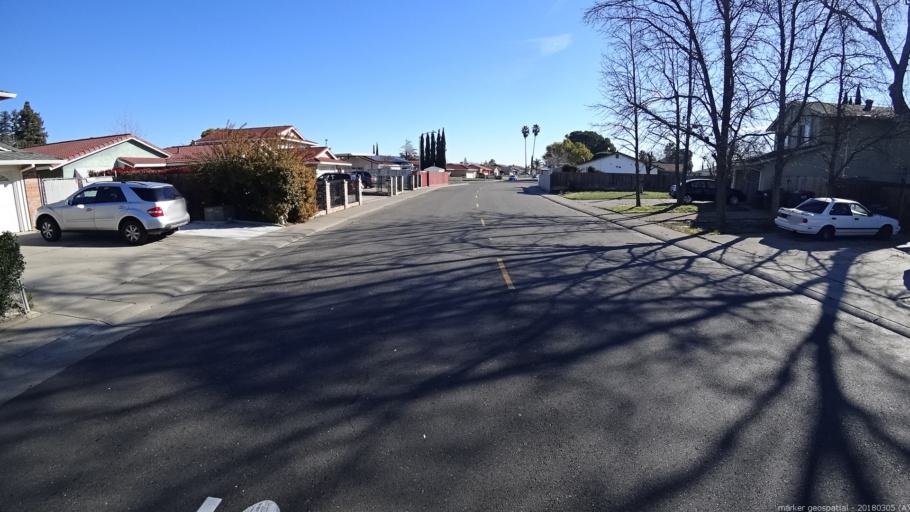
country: US
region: California
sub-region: Sacramento County
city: Florin
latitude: 38.4877
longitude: -121.4139
